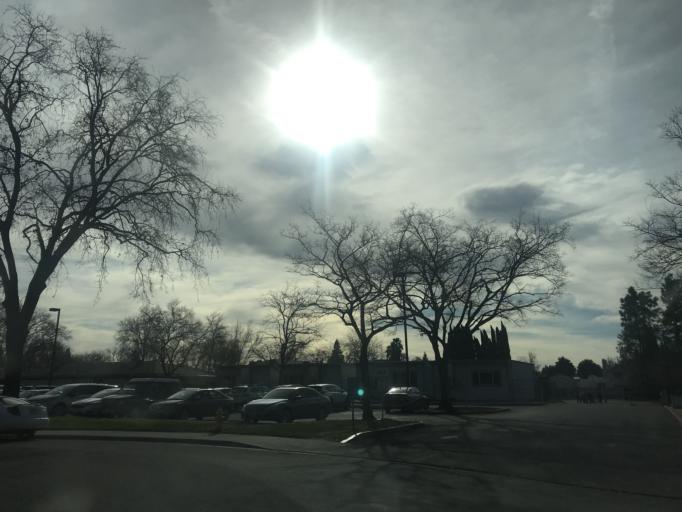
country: US
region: California
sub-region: Yolo County
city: Woodland
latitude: 38.6662
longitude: -121.7551
